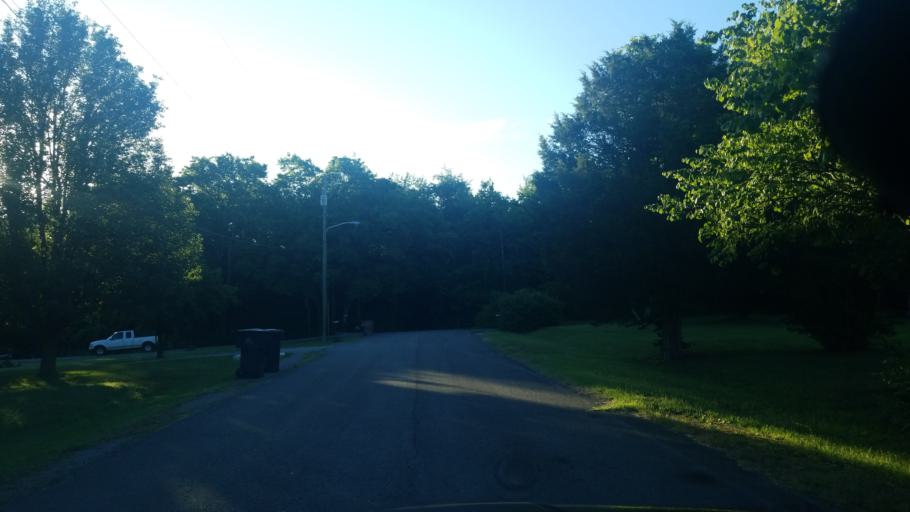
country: US
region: Tennessee
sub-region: Davidson County
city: Nashville
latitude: 36.2279
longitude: -86.7649
